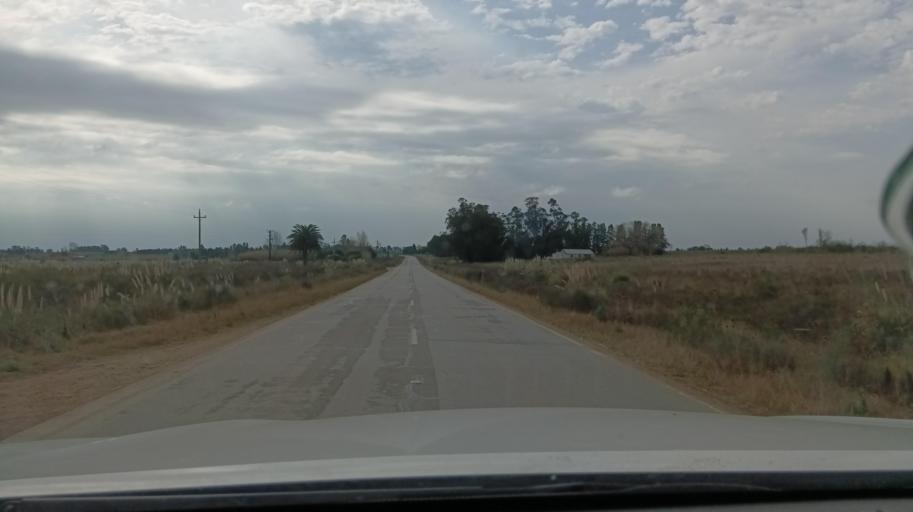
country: UY
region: Canelones
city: Sauce
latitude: -34.6492
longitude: -56.1067
